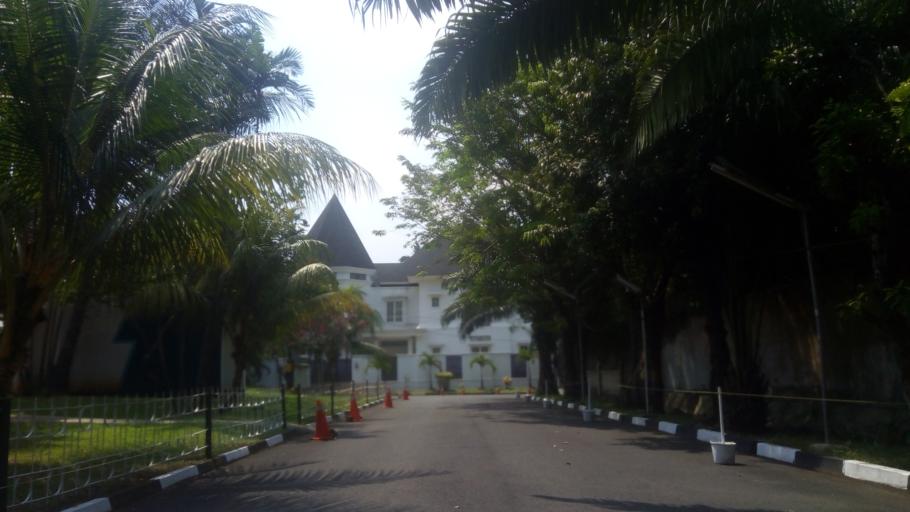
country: ID
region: Jakarta Raya
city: Jakarta
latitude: -6.2378
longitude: 106.8321
